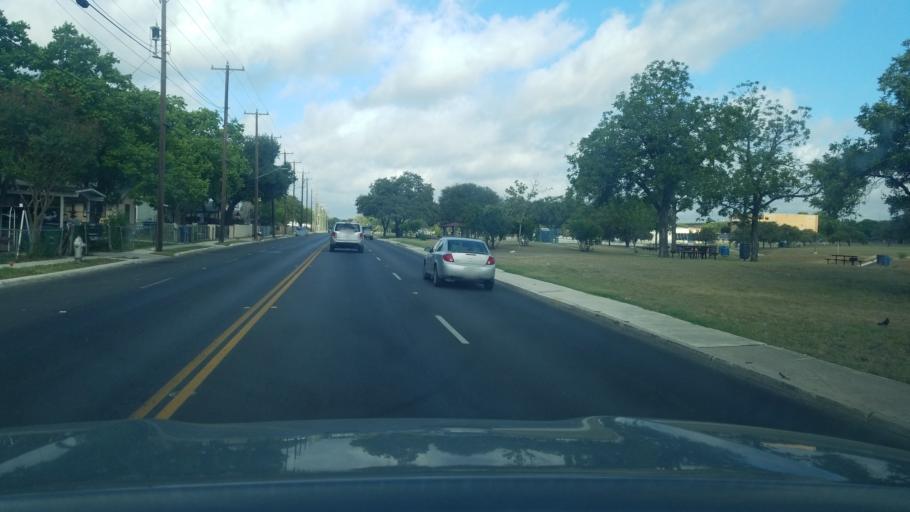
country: US
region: Texas
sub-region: Bexar County
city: San Antonio
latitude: 29.4126
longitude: -98.5218
